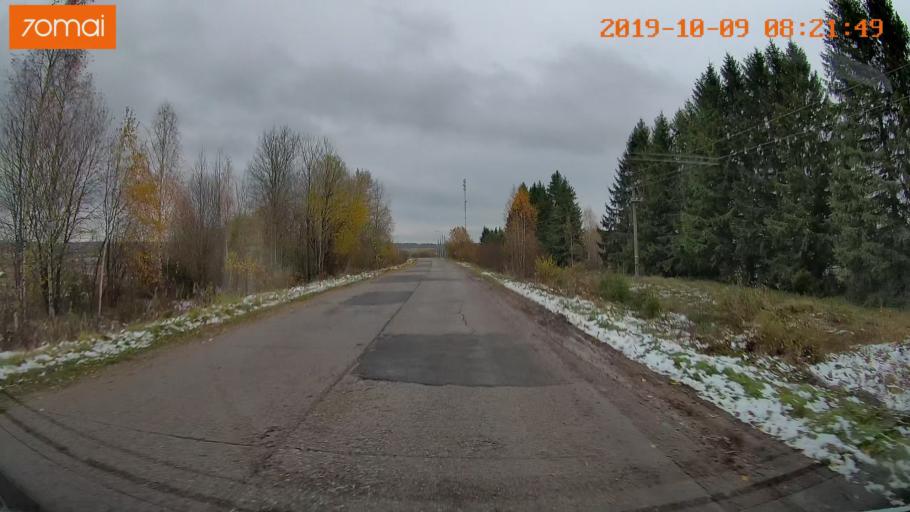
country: RU
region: Vologda
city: Gryazovets
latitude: 58.7419
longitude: 40.2833
